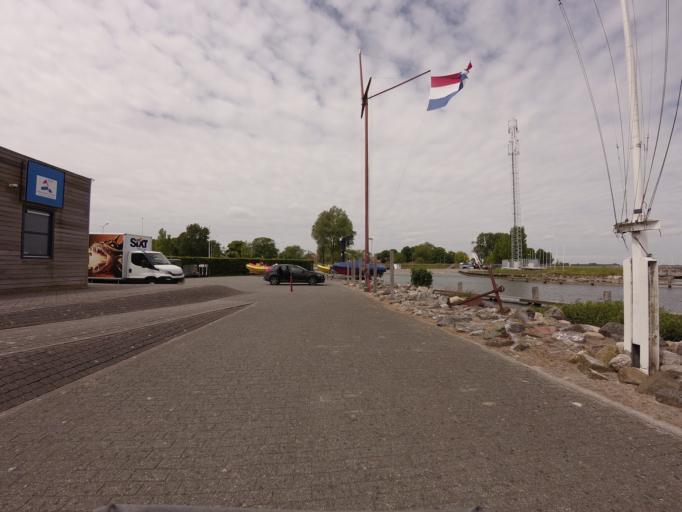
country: NL
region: North Holland
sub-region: Gemeente Medemblik
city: Medemblik
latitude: 52.7701
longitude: 5.1168
